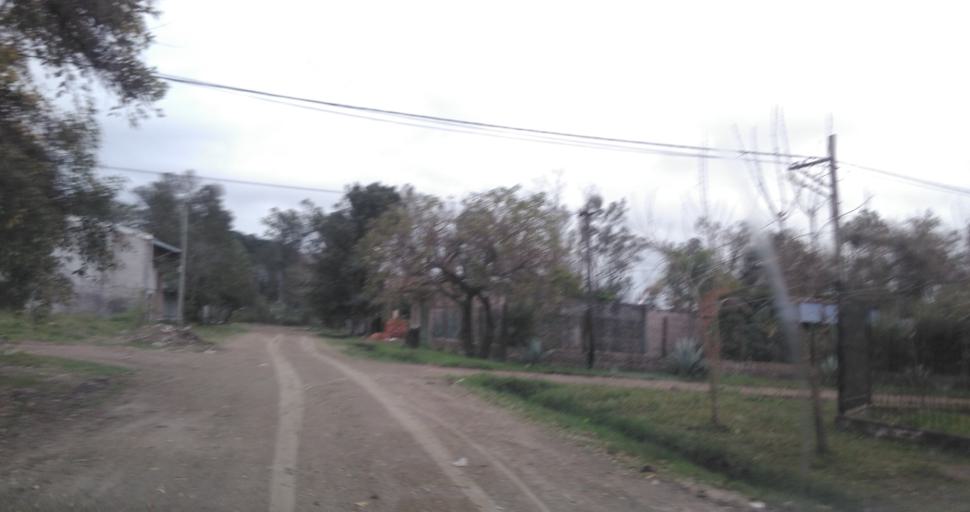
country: AR
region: Chaco
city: Fontana
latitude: -27.4436
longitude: -59.0337
